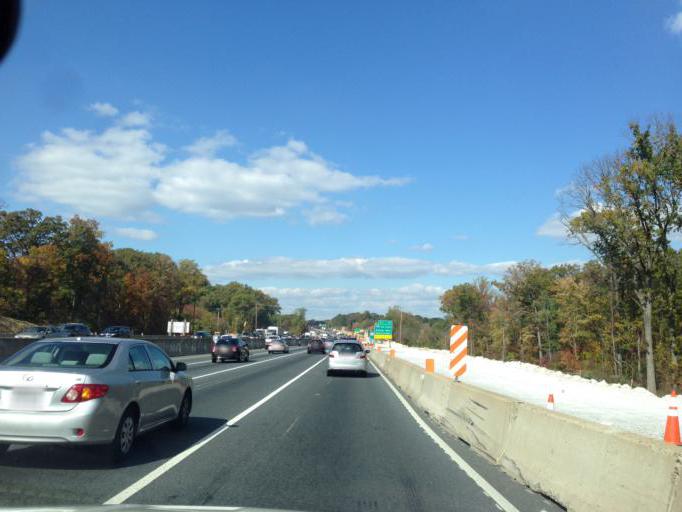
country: US
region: Maryland
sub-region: Baltimore County
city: Milford Mill
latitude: 39.3566
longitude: -76.7460
